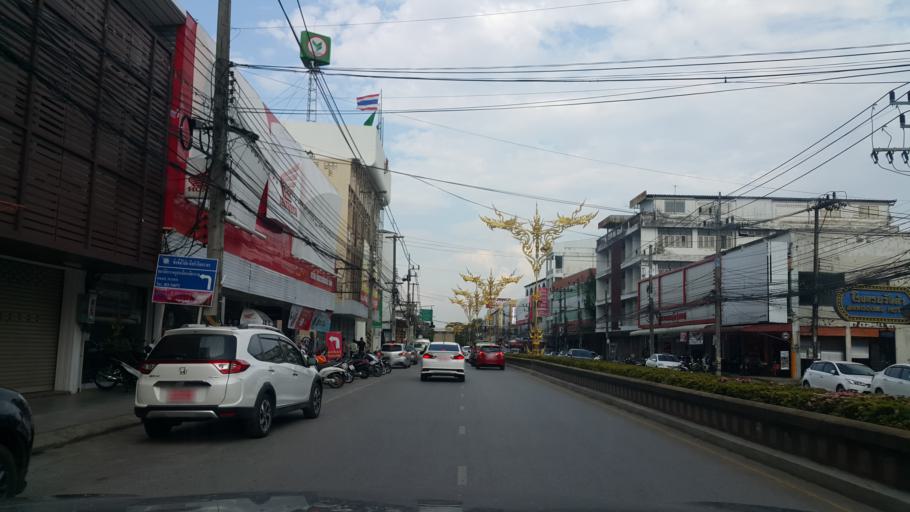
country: TH
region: Chiang Rai
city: Chiang Rai
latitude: 19.9071
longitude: 99.8315
